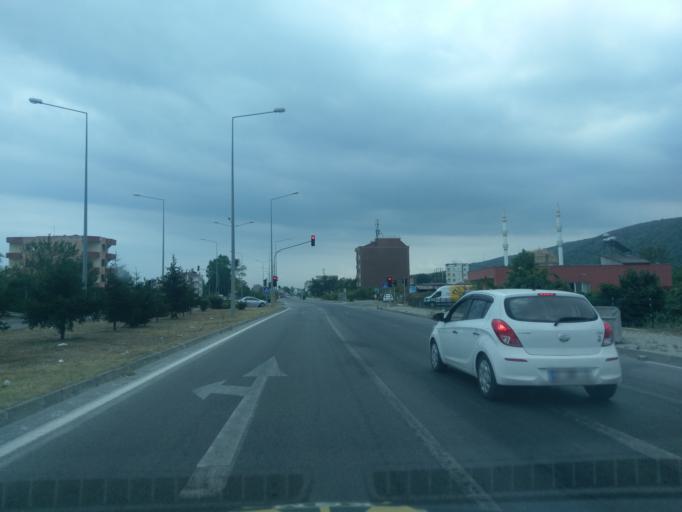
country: TR
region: Samsun
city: Taflan
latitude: 41.4042
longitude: 36.1849
